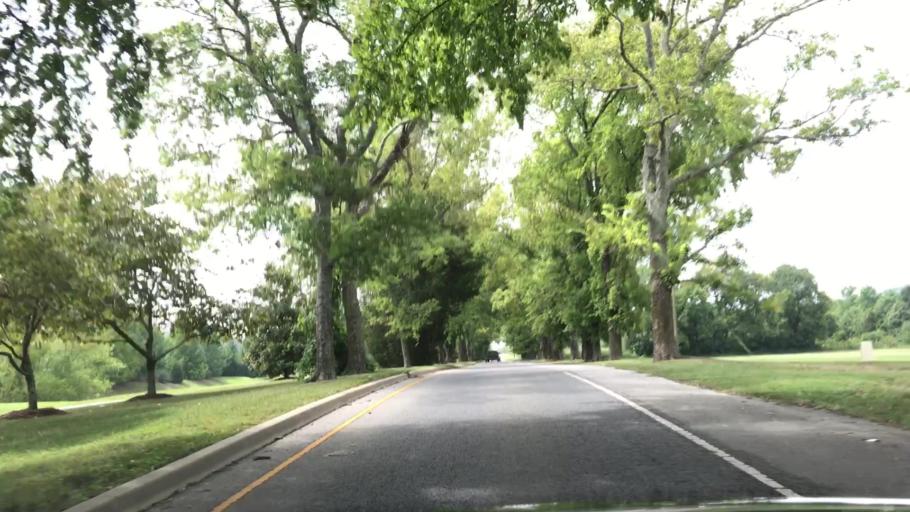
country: US
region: Tennessee
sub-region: Williamson County
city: Brentwood Estates
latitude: 35.9459
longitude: -86.7669
